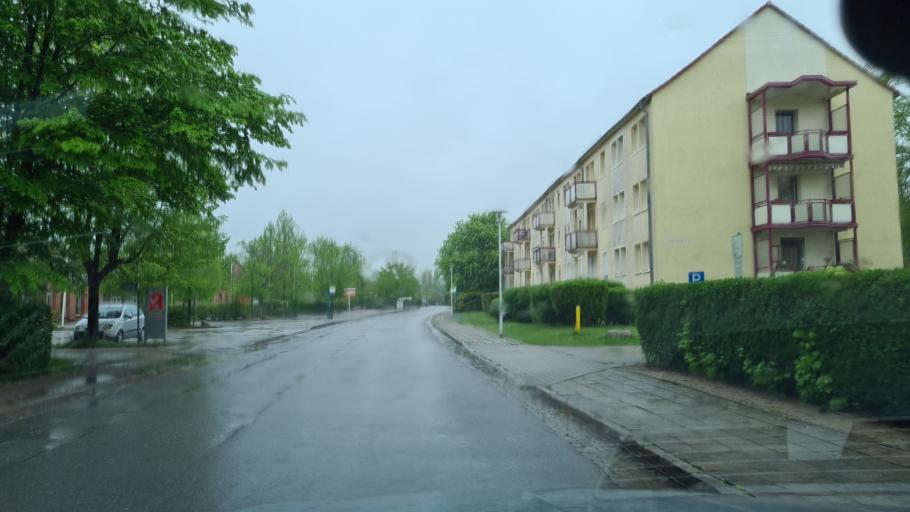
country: DE
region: Brandenburg
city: Elsterwerda
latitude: 51.4617
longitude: 13.5109
